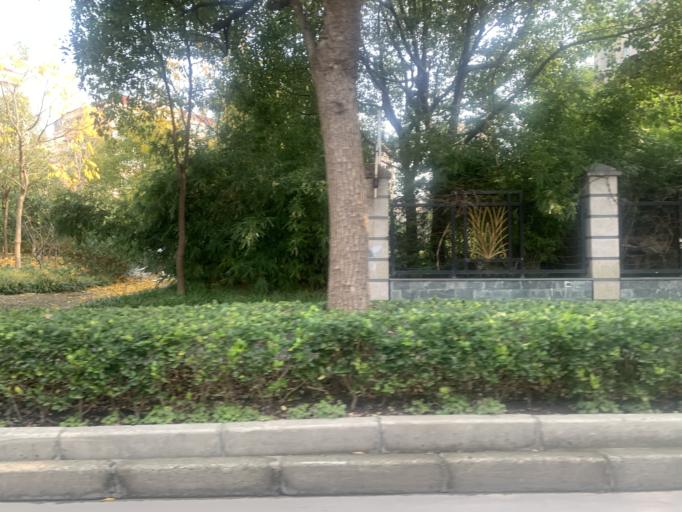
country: CN
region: Shanghai Shi
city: Huamu
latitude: 31.1832
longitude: 121.5155
